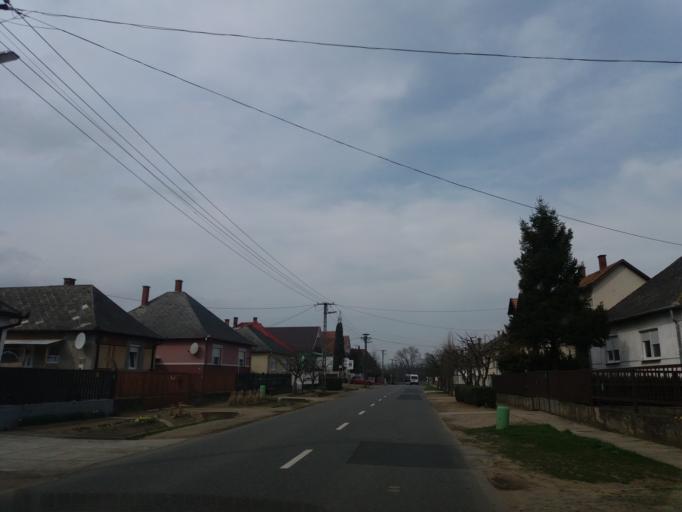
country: HU
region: Szabolcs-Szatmar-Bereg
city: Anarcs
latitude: 48.1833
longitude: 22.1015
